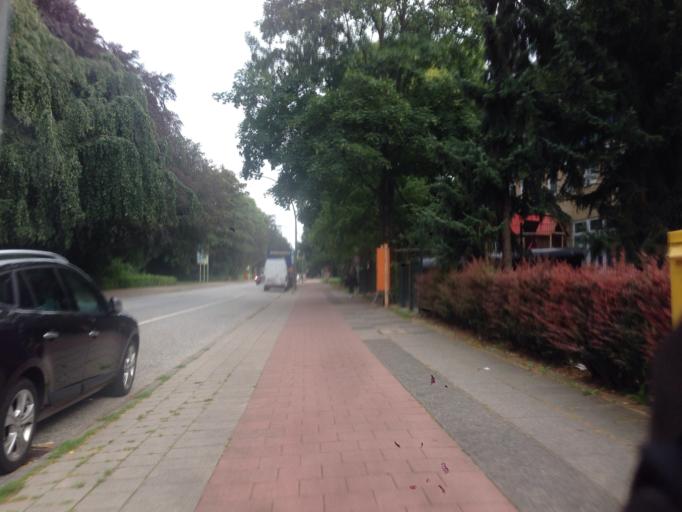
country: DE
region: Hamburg
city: Farmsen-Berne
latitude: 53.6153
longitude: 10.1143
